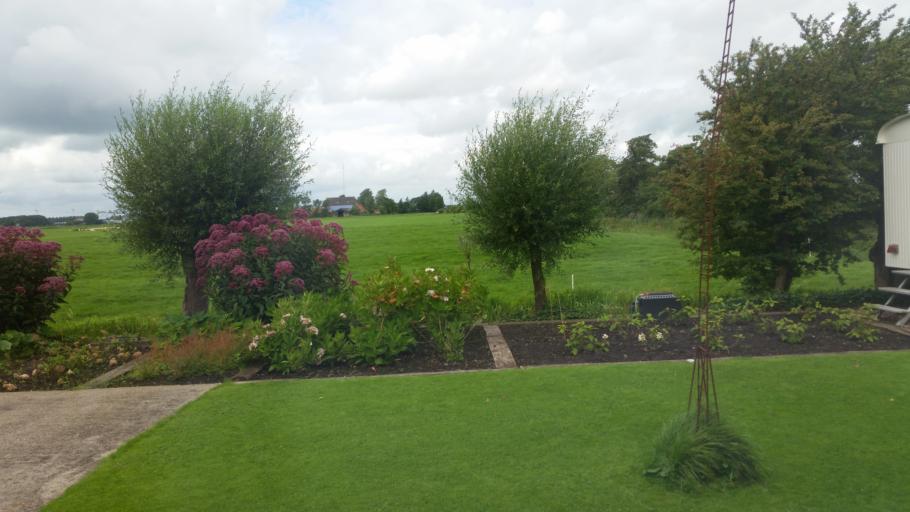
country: NL
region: Friesland
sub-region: Gemeente Boarnsterhim
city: Wergea
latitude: 53.1777
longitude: 5.8698
